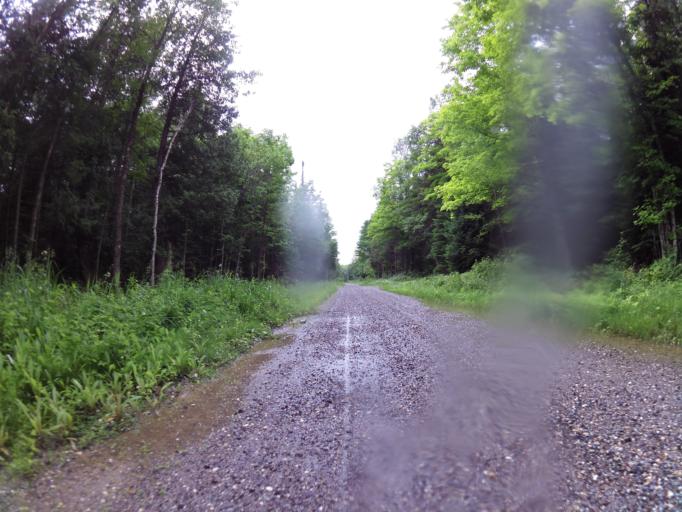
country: CA
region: Ontario
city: Renfrew
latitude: 45.0771
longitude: -76.7350
